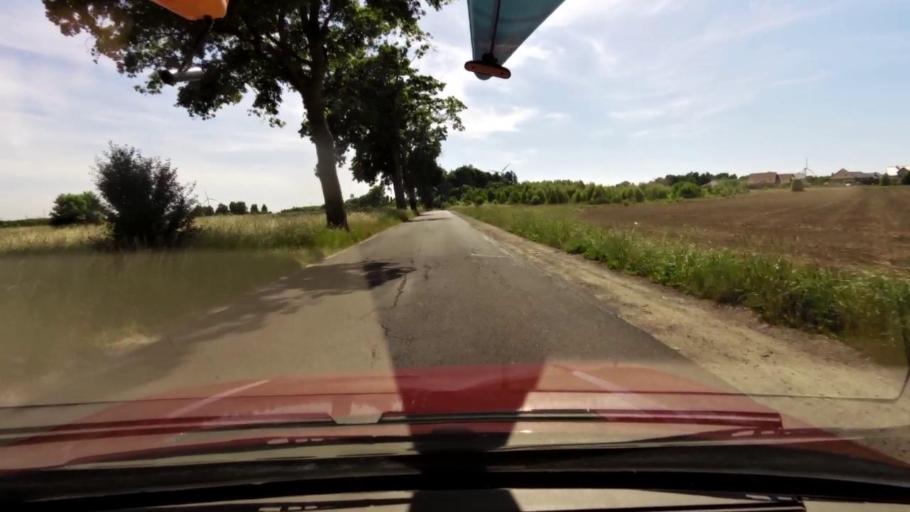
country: PL
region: Pomeranian Voivodeship
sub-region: Powiat slupski
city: Kobylnica
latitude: 54.4098
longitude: 17.0055
